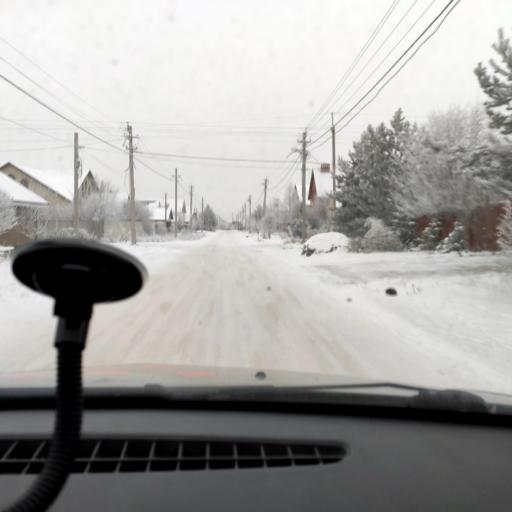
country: RU
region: Bashkortostan
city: Ufa
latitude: 54.6017
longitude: 55.9318
